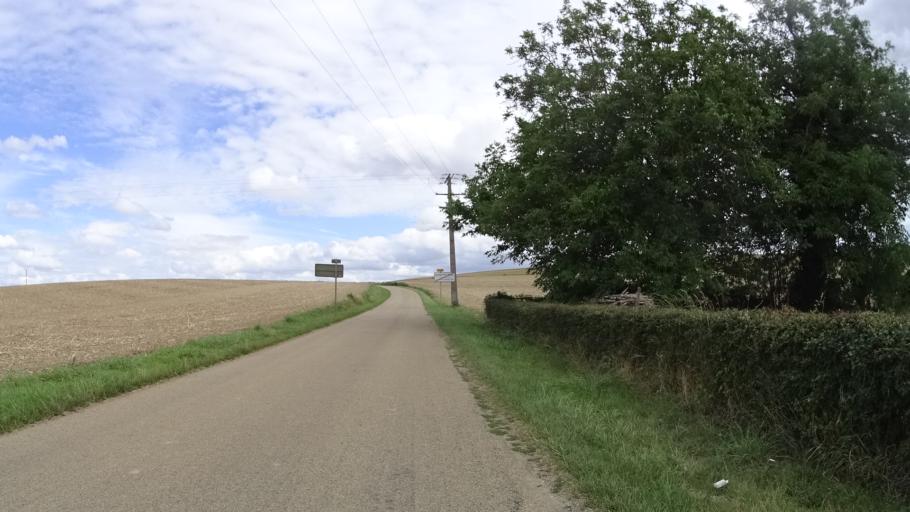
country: FR
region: Bourgogne
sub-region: Departement de l'Yonne
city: Saint-Julien-du-Sault
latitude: 47.9832
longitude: 3.2925
